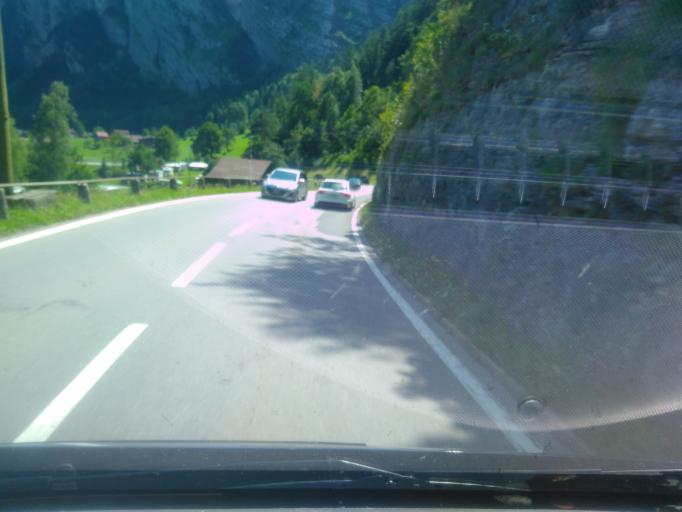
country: CH
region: Bern
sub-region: Interlaken-Oberhasli District
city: Meiringen
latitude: 46.7110
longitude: 8.2147
